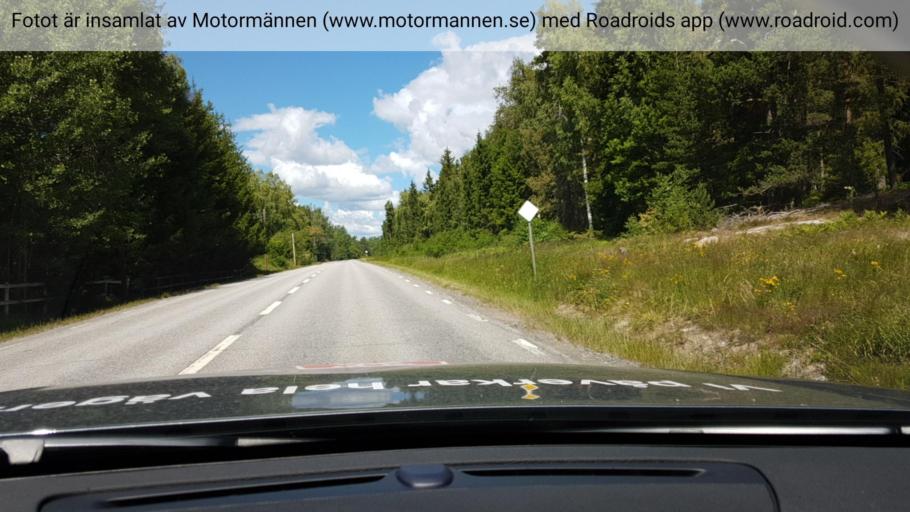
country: SE
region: Stockholm
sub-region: Varmdo Kommun
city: Hemmesta
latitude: 59.3418
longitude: 18.4822
